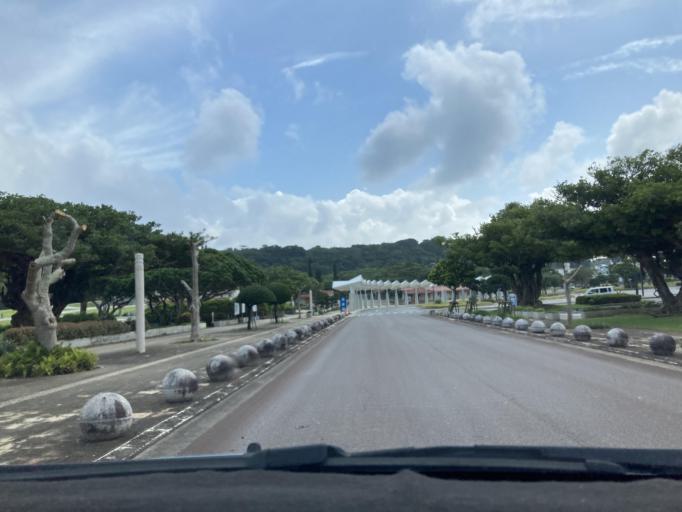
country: JP
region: Okinawa
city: Itoman
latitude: 26.0964
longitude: 127.7227
